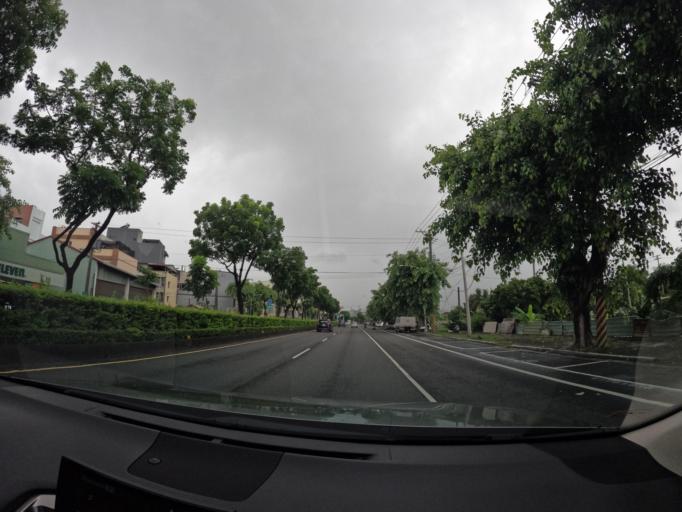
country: TW
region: Taiwan
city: Fengshan
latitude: 22.6359
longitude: 120.3762
